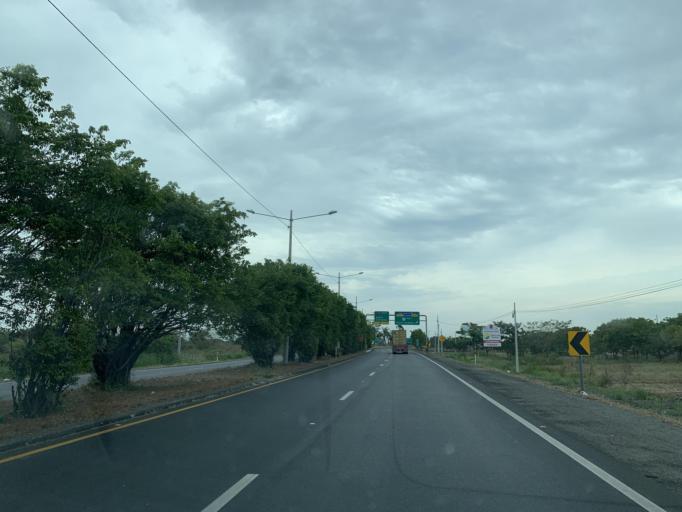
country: EC
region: Guayas
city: Eloy Alfaro
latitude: -2.1996
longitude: -79.7618
